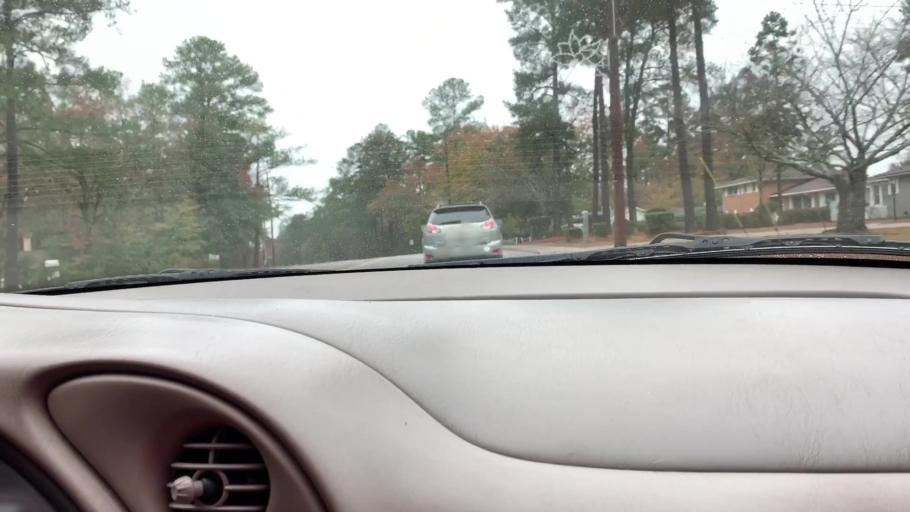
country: US
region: South Carolina
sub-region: Richland County
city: Forest Acres
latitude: 34.0306
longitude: -80.9662
